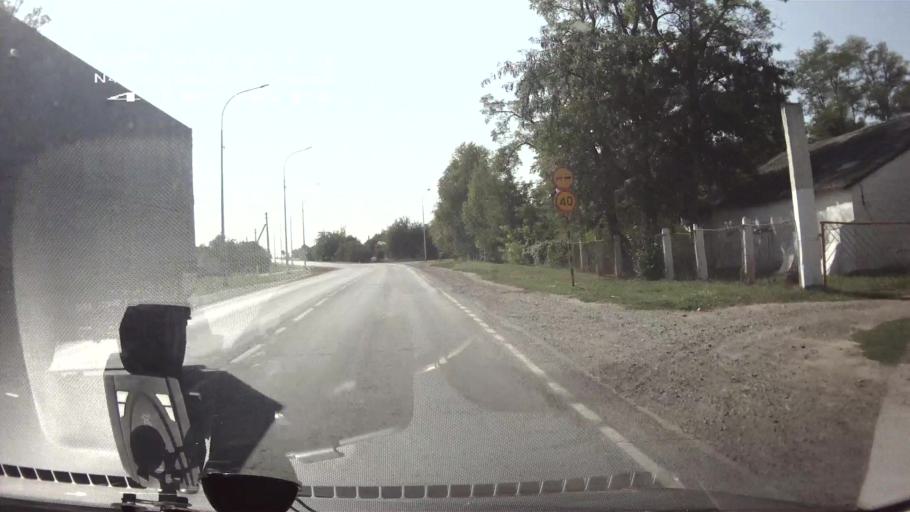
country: RU
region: Krasnodarskiy
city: Dmitriyevskaya
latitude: 45.7181
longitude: 40.7233
